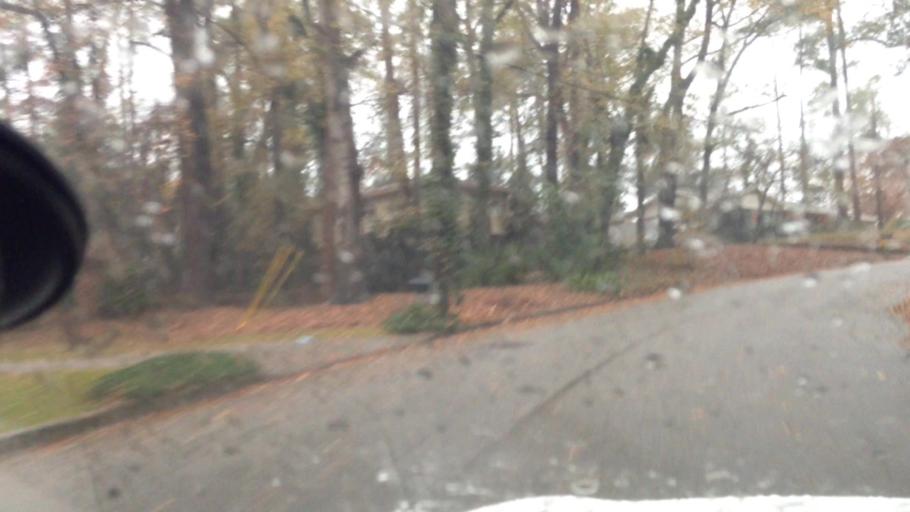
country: US
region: South Carolina
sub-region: Aiken County
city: North Augusta
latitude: 33.5033
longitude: -81.9868
